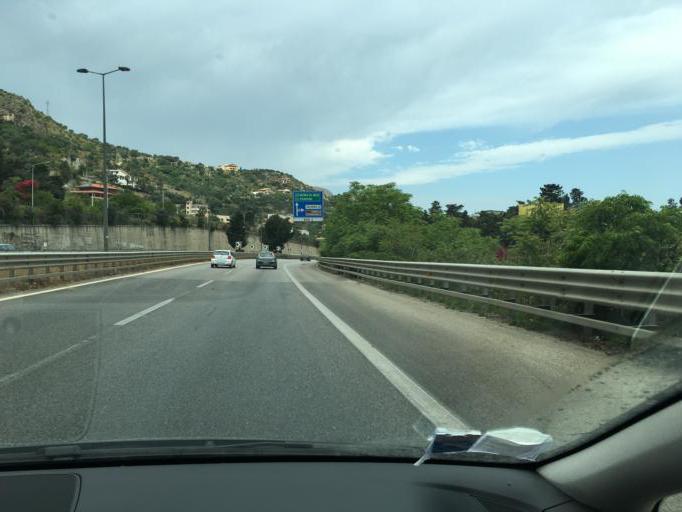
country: IT
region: Sicily
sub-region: Palermo
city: Isola delle Femmine
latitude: 38.1870
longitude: 13.2863
